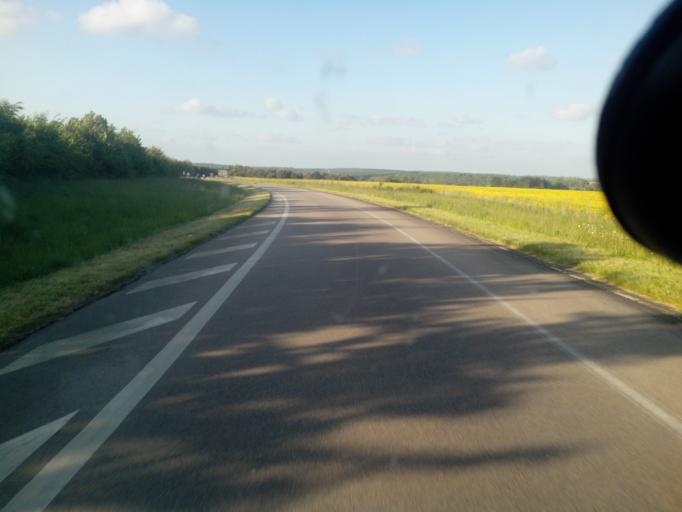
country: FR
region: Haute-Normandie
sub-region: Departement de la Seine-Maritime
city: Saint-Saens
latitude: 49.6510
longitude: 1.2681
